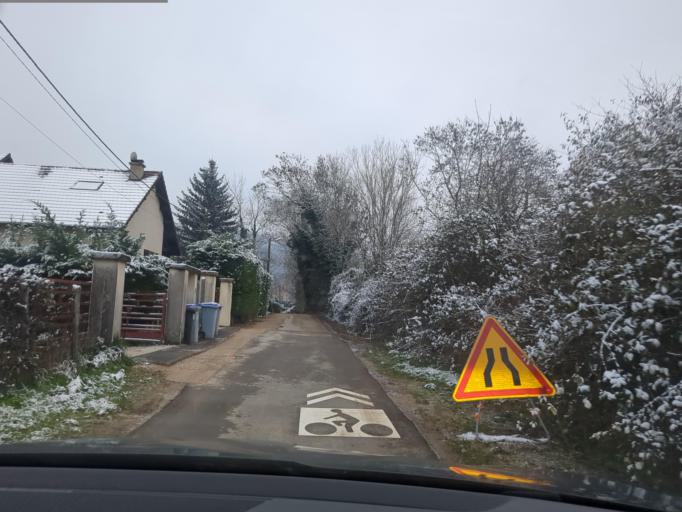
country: FR
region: Franche-Comte
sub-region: Departement du Jura
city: Perrigny
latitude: 46.6611
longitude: 5.5858
